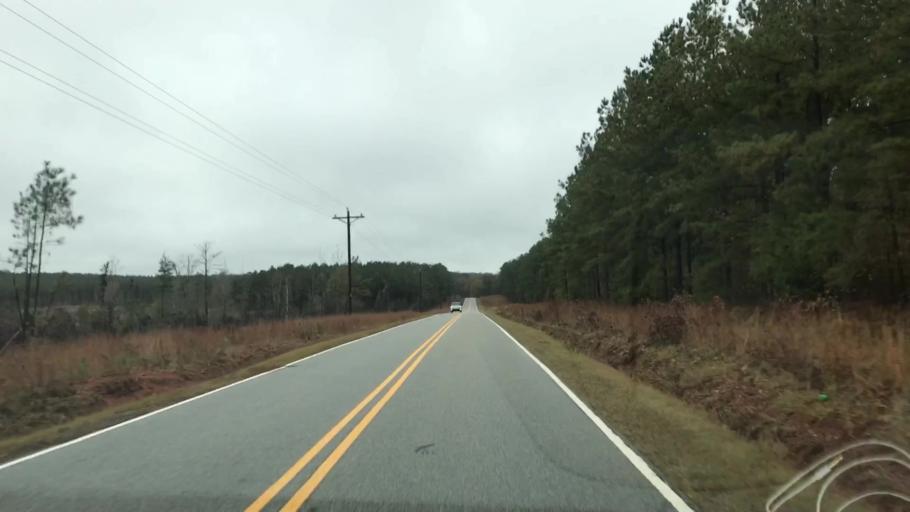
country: US
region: South Carolina
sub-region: Laurens County
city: Joanna
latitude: 34.3147
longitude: -81.9389
